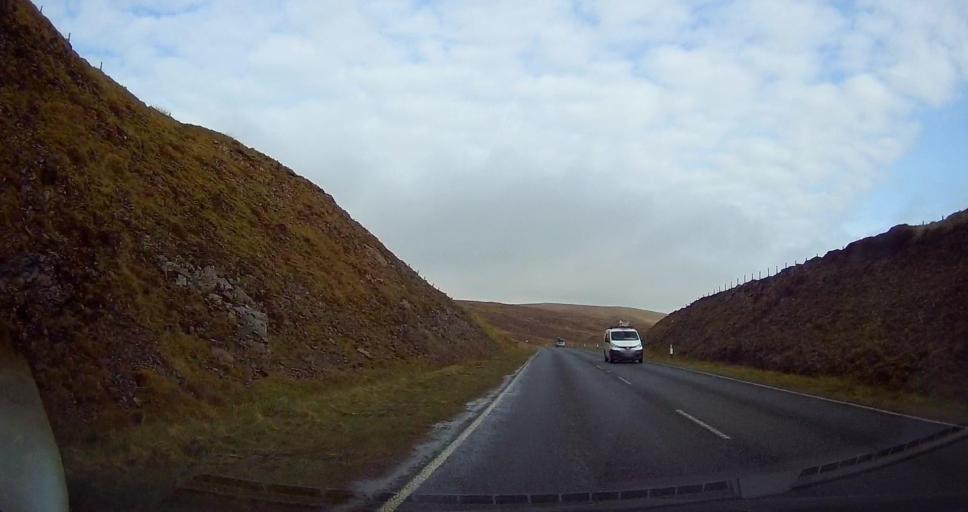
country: GB
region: Scotland
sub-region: Shetland Islands
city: Sandwick
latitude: 60.0679
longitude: -1.2259
